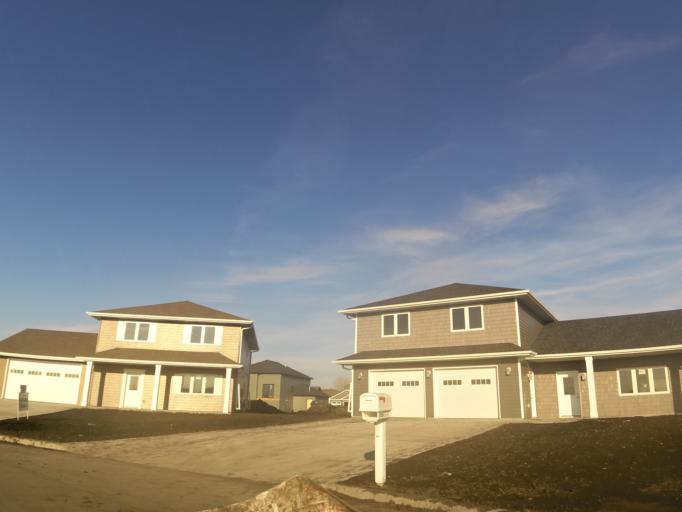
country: US
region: North Dakota
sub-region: Grand Forks County
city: Grand Forks
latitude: 47.8669
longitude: -97.0358
